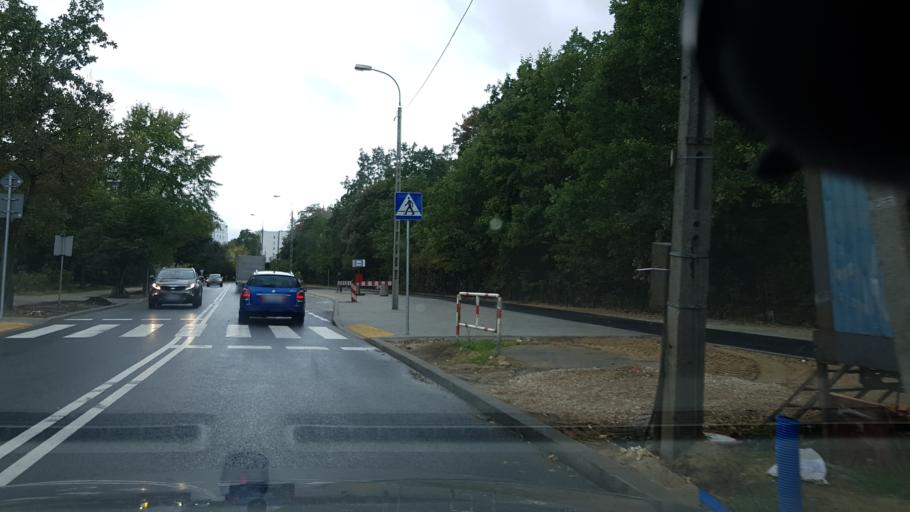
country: PL
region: Masovian Voivodeship
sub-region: Warszawa
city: Zoliborz
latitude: 52.2853
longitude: 20.9705
